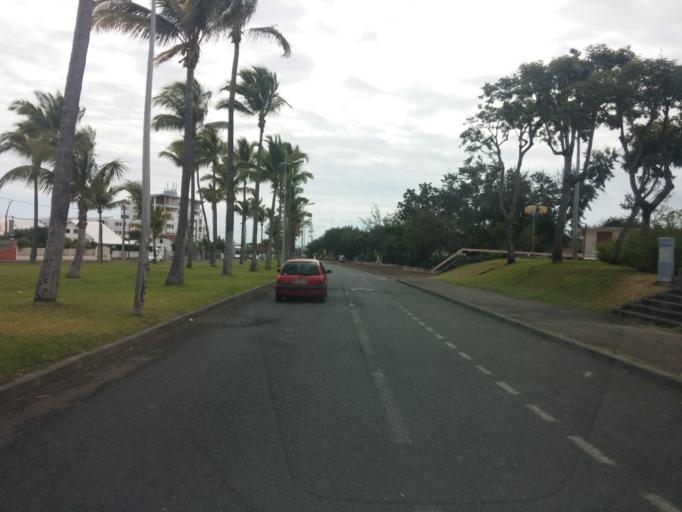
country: RE
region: Reunion
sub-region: Reunion
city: Le Port
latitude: -20.9476
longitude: 55.2936
